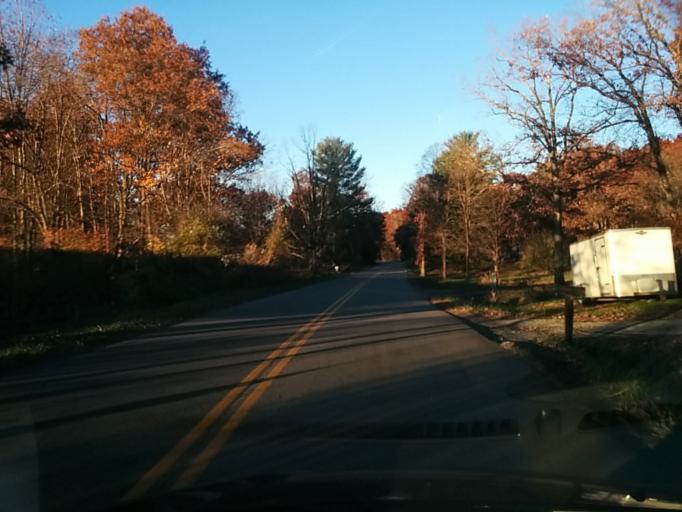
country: US
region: Virginia
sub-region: Rockbridge County
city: East Lexington
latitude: 37.9715
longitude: -79.5096
